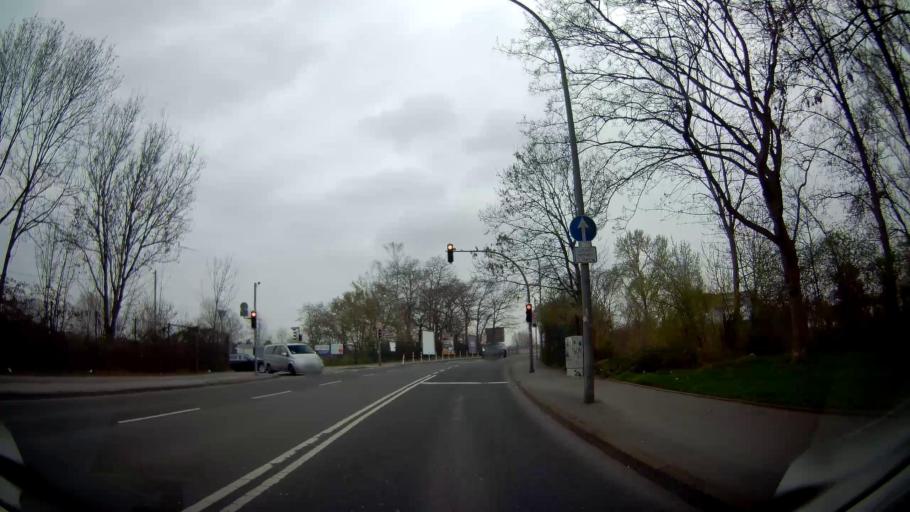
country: DE
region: North Rhine-Westphalia
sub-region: Regierungsbezirk Arnsberg
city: Dortmund
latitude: 51.5230
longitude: 7.4877
